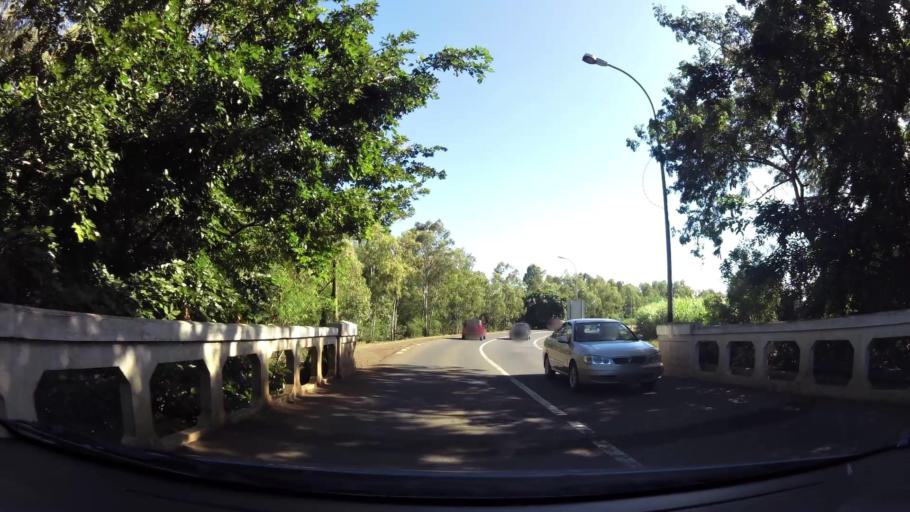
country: MU
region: Black River
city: Cascavelle
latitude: -20.3146
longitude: 57.4039
